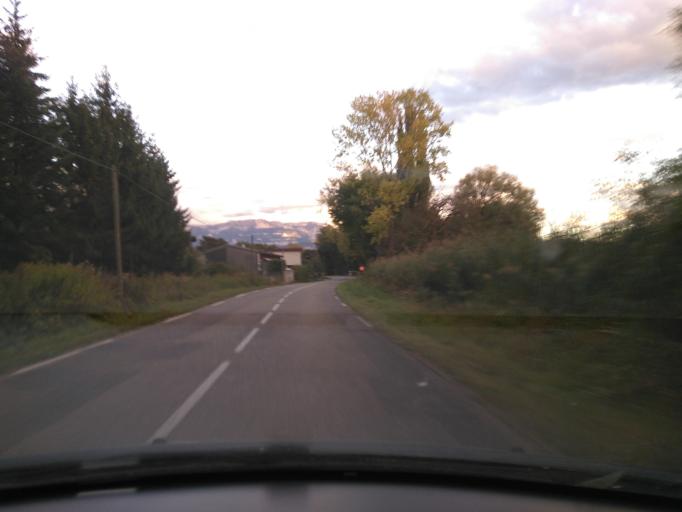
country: FR
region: Rhone-Alpes
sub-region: Departement de l'Isere
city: Saint-Cassien
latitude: 45.3677
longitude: 5.5447
